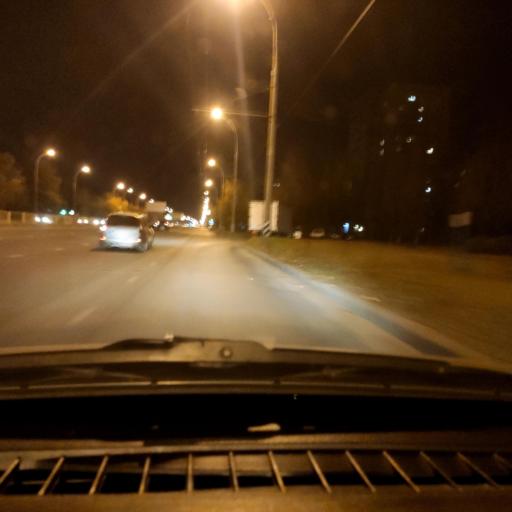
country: RU
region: Samara
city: Tol'yatti
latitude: 53.5285
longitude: 49.2975
